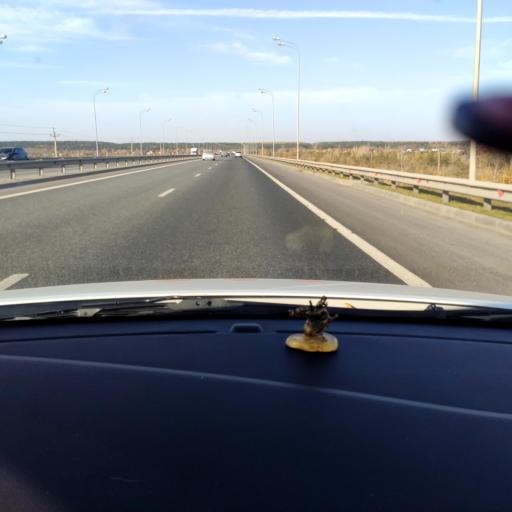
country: RU
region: Tatarstan
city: Osinovo
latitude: 55.8072
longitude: 48.8419
